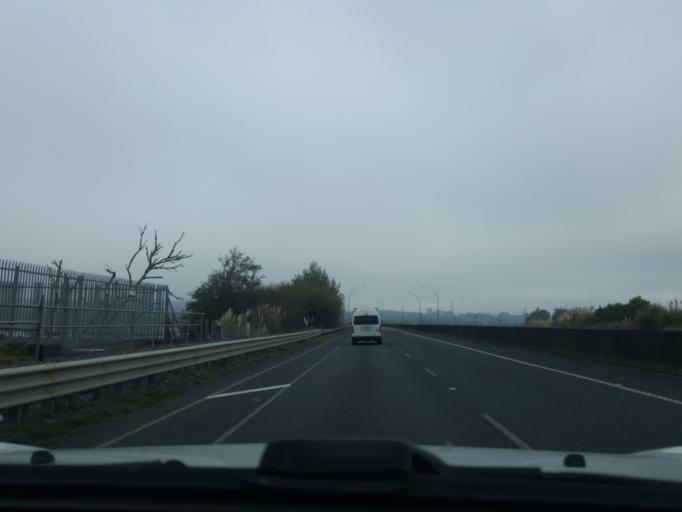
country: NZ
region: Waikato
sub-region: Waikato District
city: Te Kauwhata
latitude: -37.3133
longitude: 175.0667
